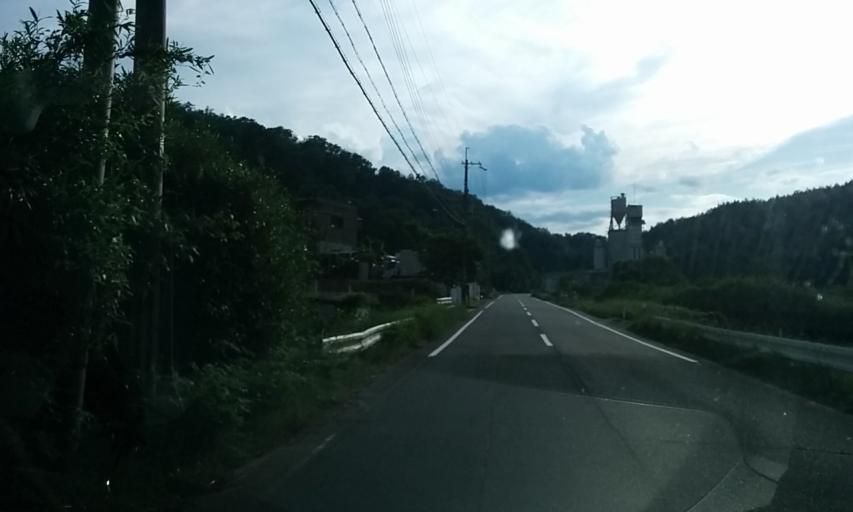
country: JP
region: Kyoto
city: Ayabe
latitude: 35.2016
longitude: 135.3814
